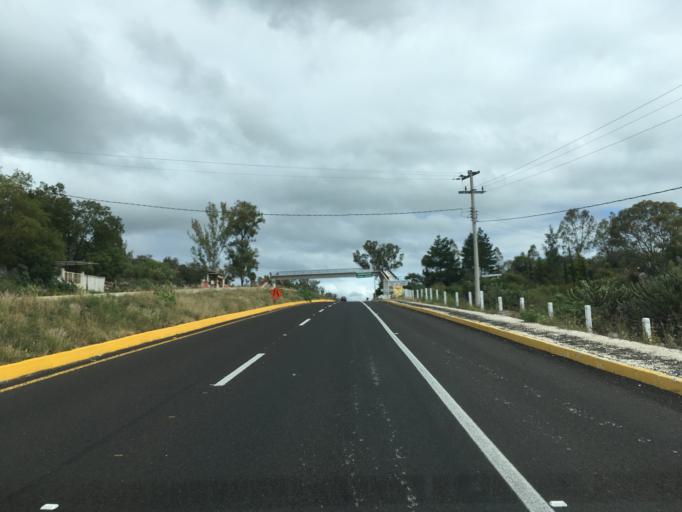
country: MX
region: Hidalgo
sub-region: Atotonilco el Grande
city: Santa Maria Amajac
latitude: 20.3971
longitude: -98.7193
